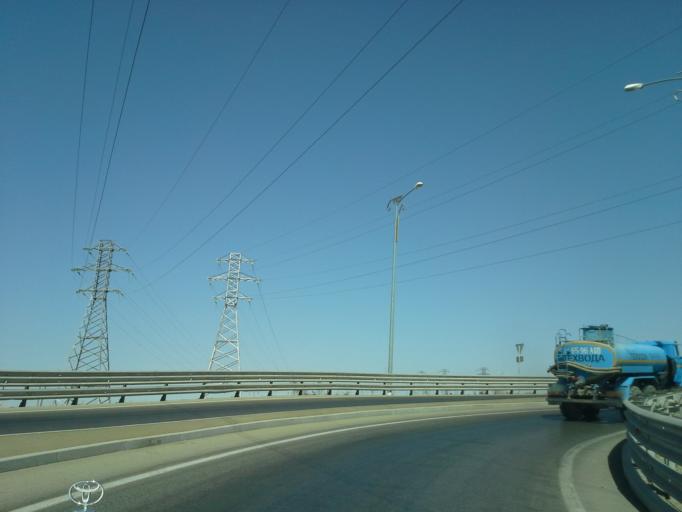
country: TM
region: Ahal
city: Annau
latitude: 37.9142
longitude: 58.4829
